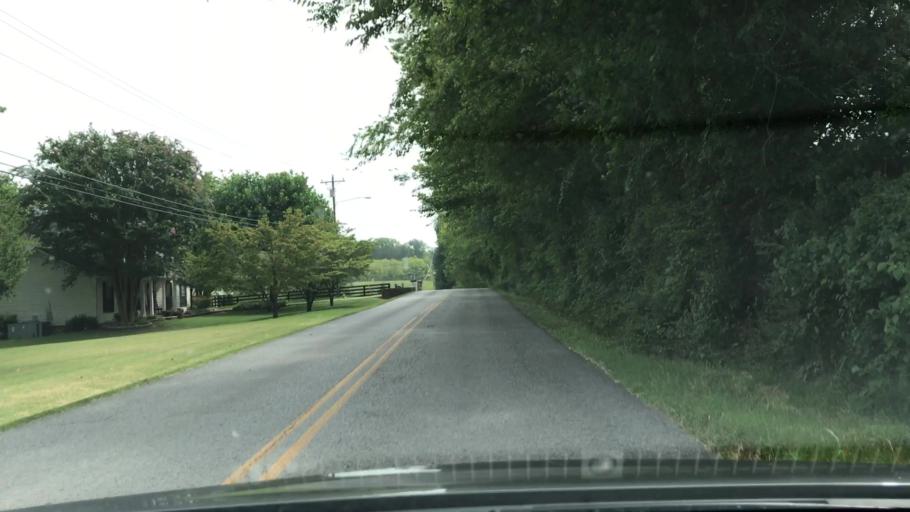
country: US
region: Tennessee
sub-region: Rutherford County
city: La Vergne
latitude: 35.9744
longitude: -86.5978
